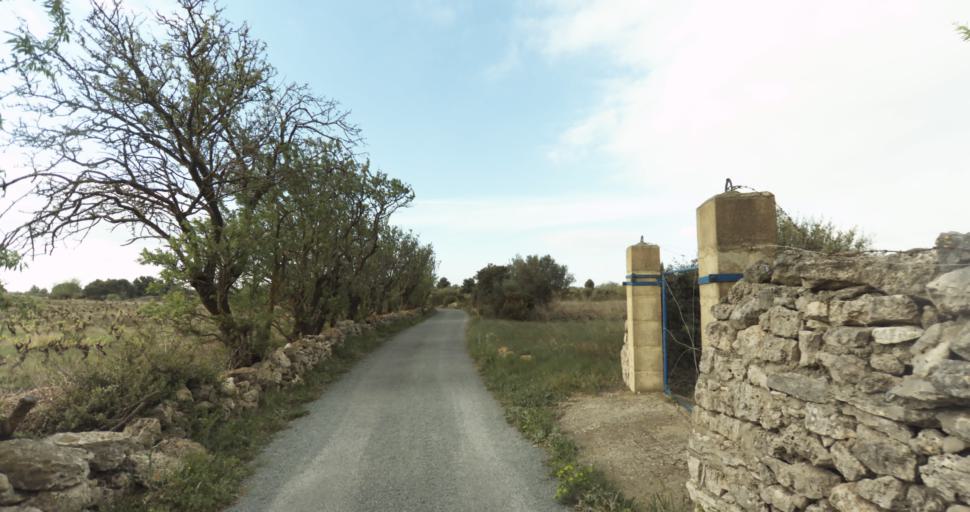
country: FR
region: Languedoc-Roussillon
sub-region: Departement de l'Aude
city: Leucate
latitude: 42.9227
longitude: 3.0262
